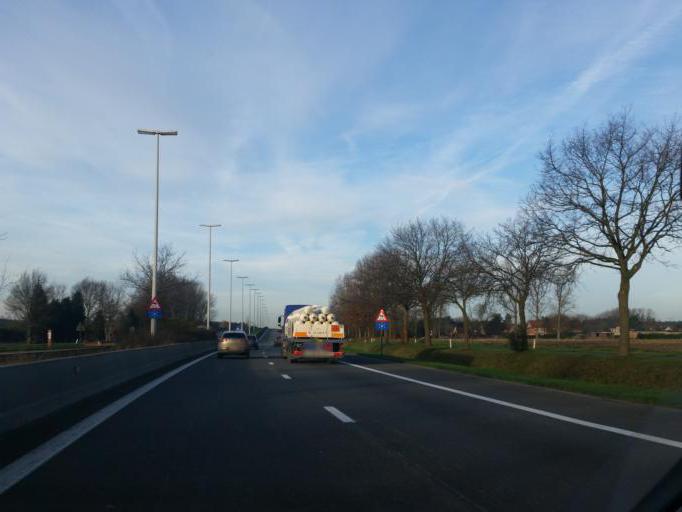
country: BE
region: Flanders
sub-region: Provincie Oost-Vlaanderen
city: Wachtebeke
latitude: 51.1866
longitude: 3.8619
